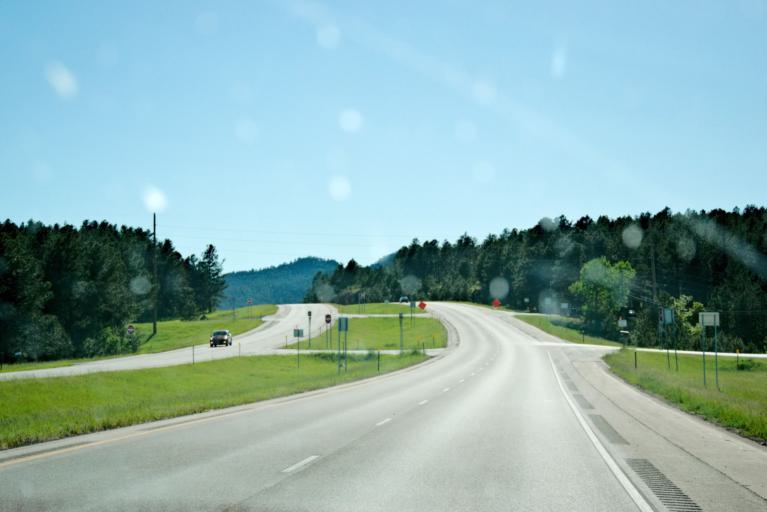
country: US
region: South Dakota
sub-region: Pennington County
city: Colonial Pine Hills
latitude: 43.9687
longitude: -103.3435
